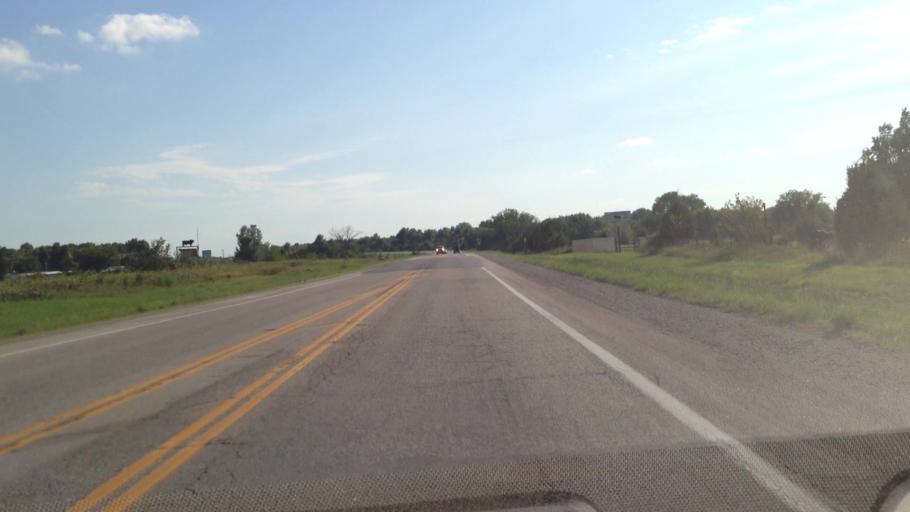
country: US
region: Kansas
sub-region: Crawford County
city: Arma
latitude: 37.5541
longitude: -94.7067
